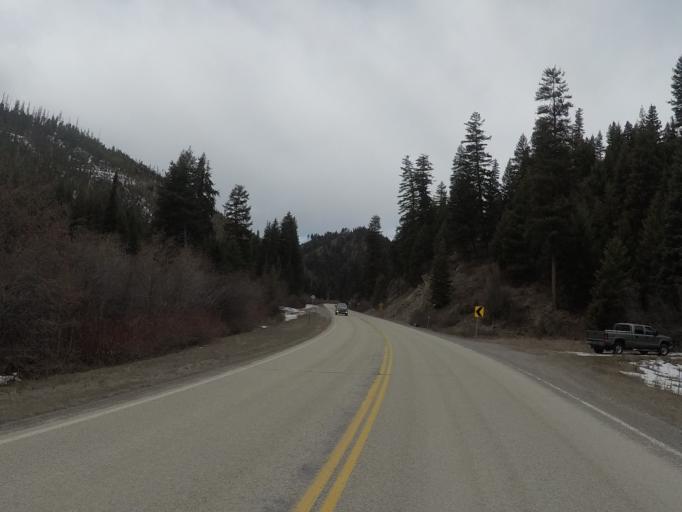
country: US
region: Montana
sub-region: Missoula County
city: Frenchtown
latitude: 46.7812
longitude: -114.4100
